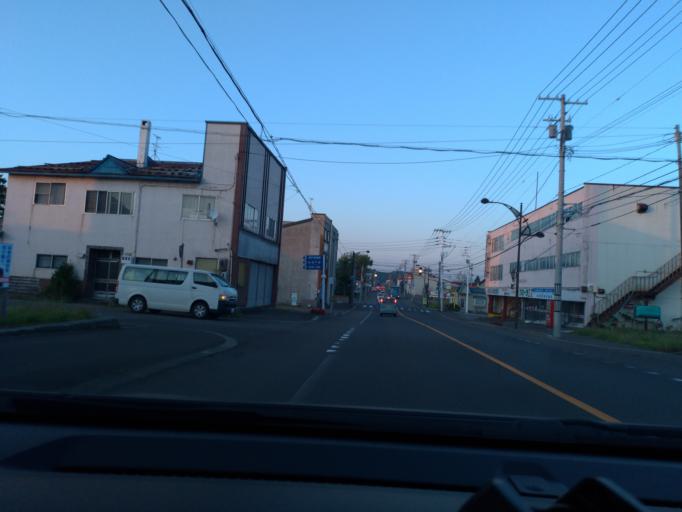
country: JP
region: Hokkaido
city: Iwamizawa
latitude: 43.3370
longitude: 141.6724
